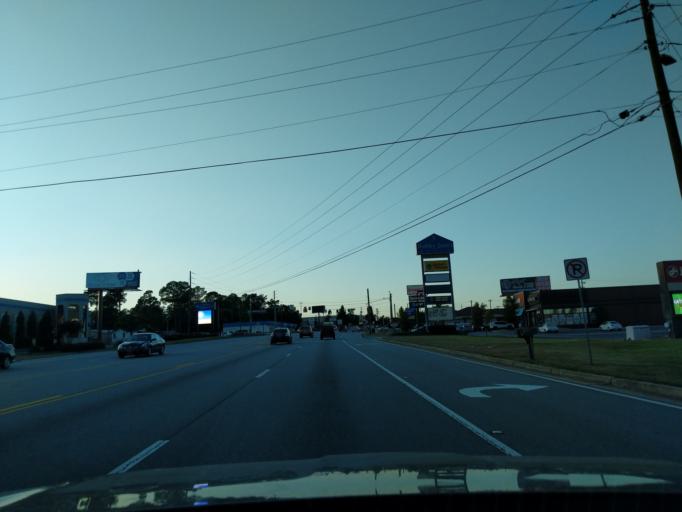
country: US
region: Georgia
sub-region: Columbia County
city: Martinez
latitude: 33.5074
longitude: -82.0925
